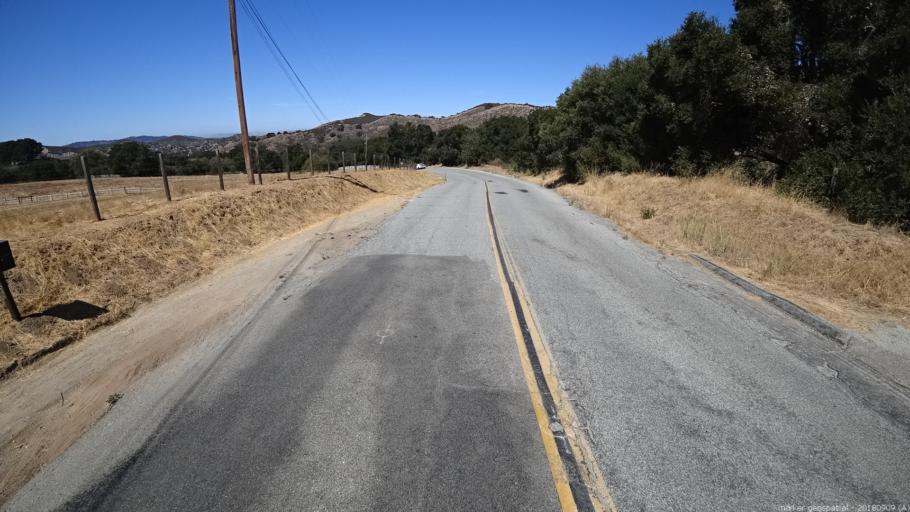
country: US
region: California
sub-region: Monterey County
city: Carmel Valley Village
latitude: 36.5507
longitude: -121.6734
